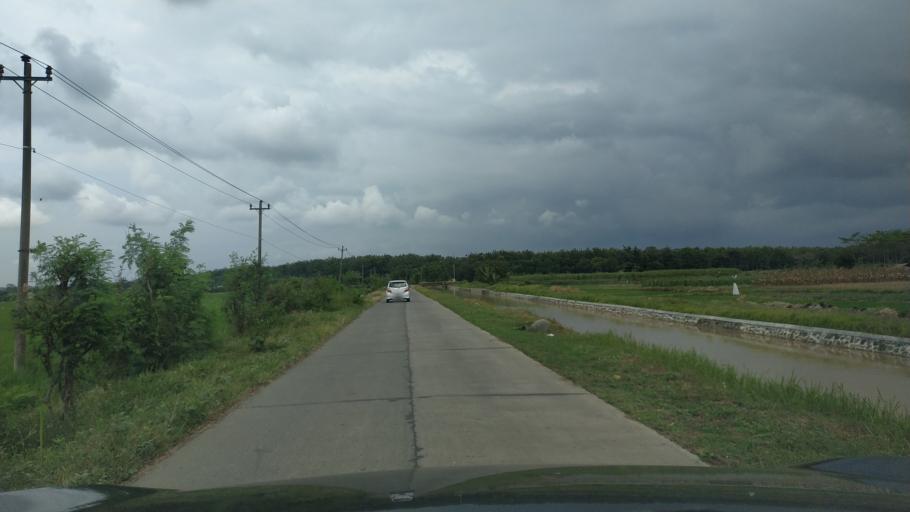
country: ID
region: Central Java
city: Pemalang
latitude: -6.9510
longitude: 109.3580
